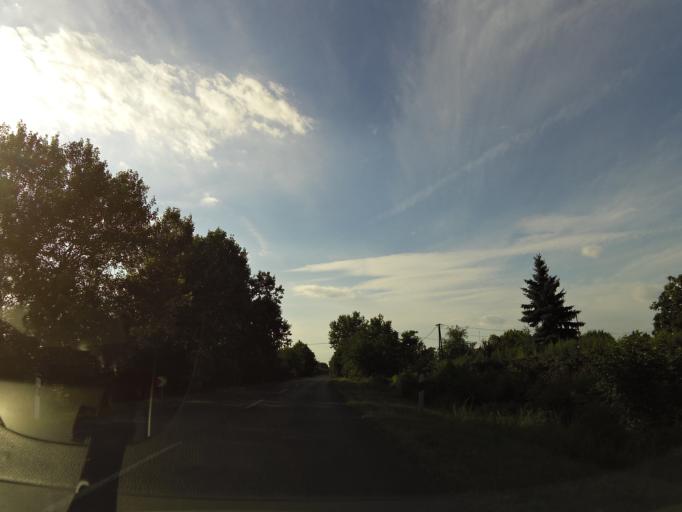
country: HU
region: Csongrad
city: Szatymaz
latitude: 46.3530
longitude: 20.0558
